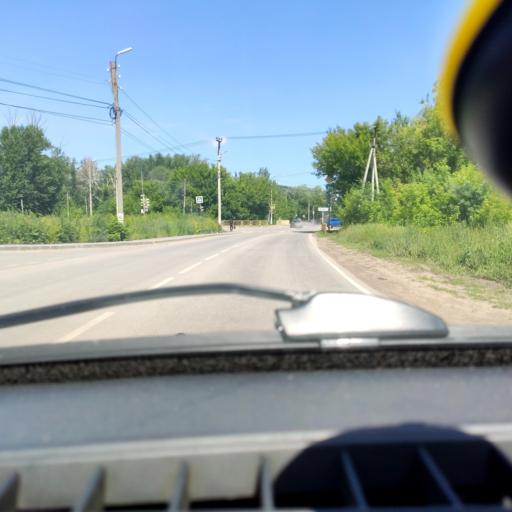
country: RU
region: Samara
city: Zhigulevsk
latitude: 53.3969
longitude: 49.5095
